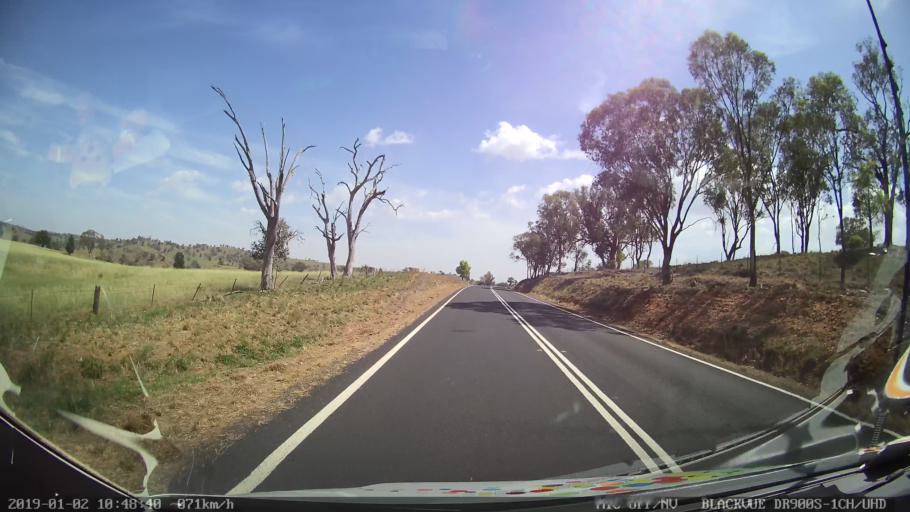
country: AU
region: New South Wales
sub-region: Cootamundra
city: Cootamundra
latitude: -34.7342
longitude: 148.2777
